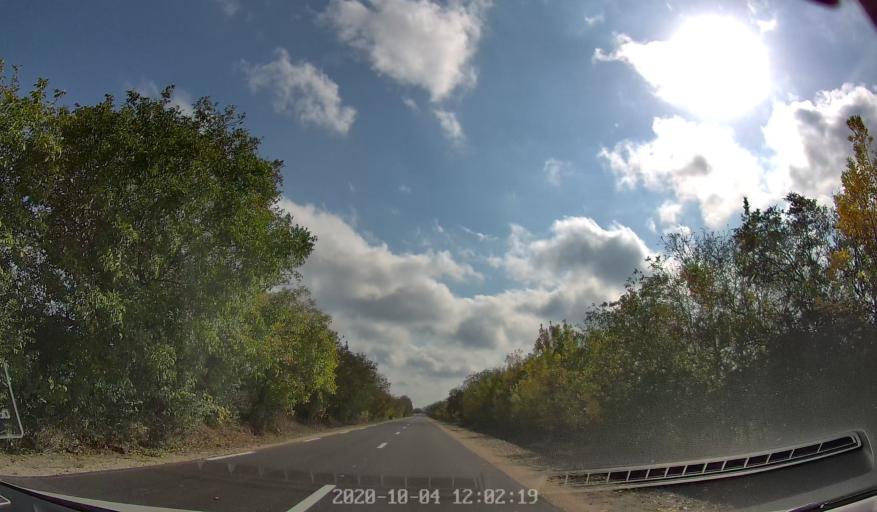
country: MD
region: Rezina
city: Saharna
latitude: 47.6179
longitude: 28.9048
